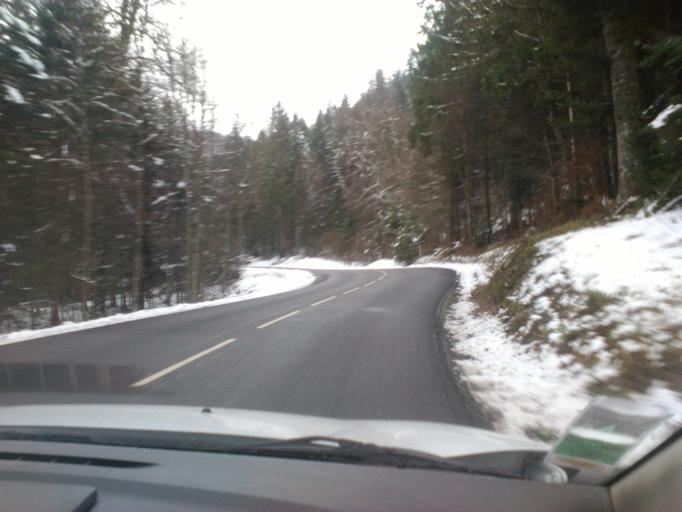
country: FR
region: Lorraine
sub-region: Departement des Vosges
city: Xonrupt-Longemer
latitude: 48.0481
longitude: 6.9943
